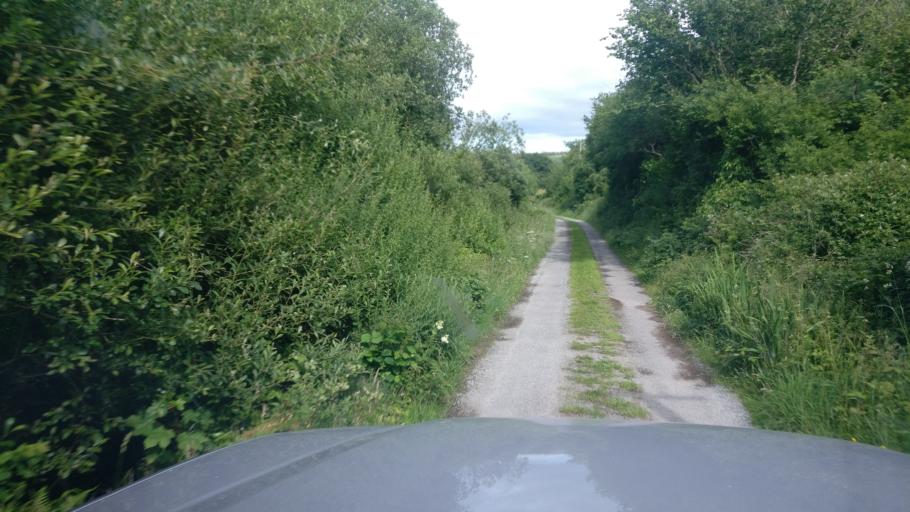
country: IE
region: Connaught
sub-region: County Galway
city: Gort
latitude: 53.1048
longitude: -8.6949
